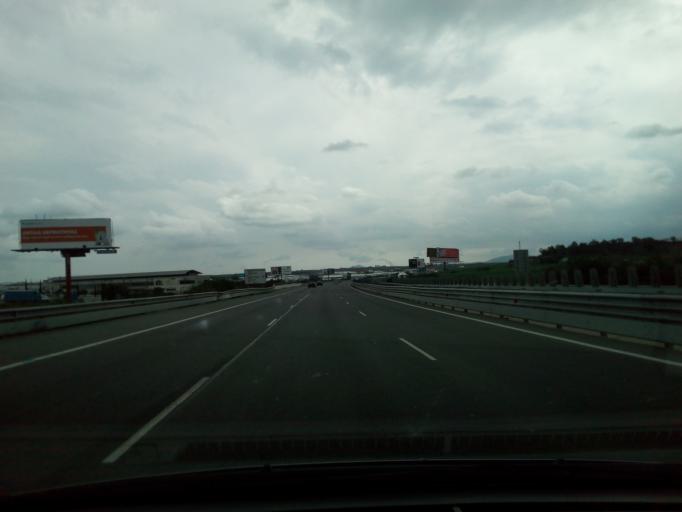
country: CY
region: Lefkosia
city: Dali
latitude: 35.0577
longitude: 33.3845
